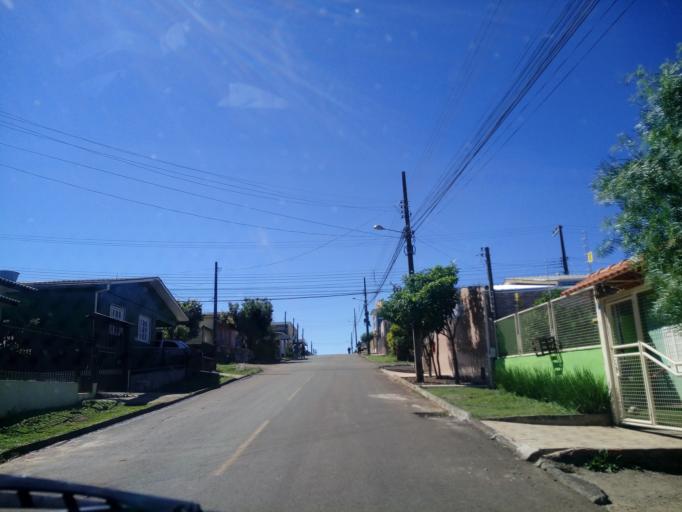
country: BR
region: Santa Catarina
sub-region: Chapeco
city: Chapeco
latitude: -27.0890
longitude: -52.6770
